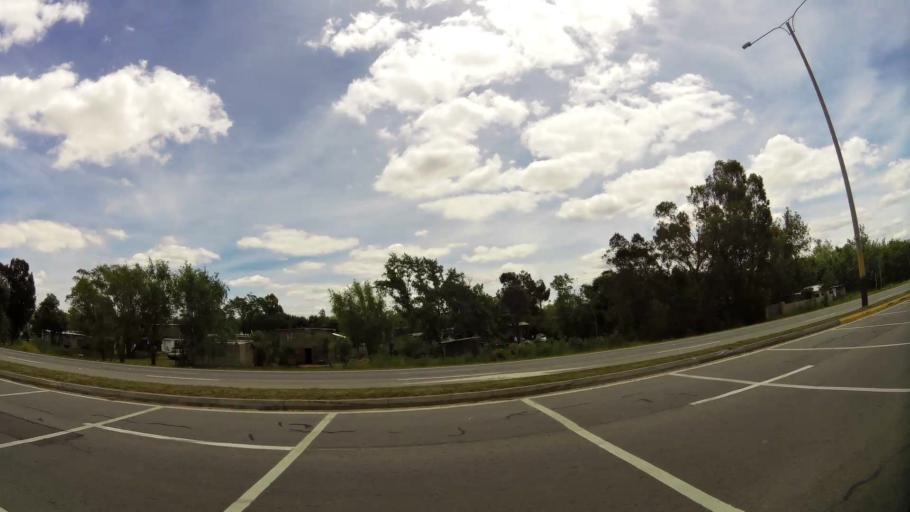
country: UY
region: Canelones
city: Pando
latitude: -34.8030
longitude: -55.9537
